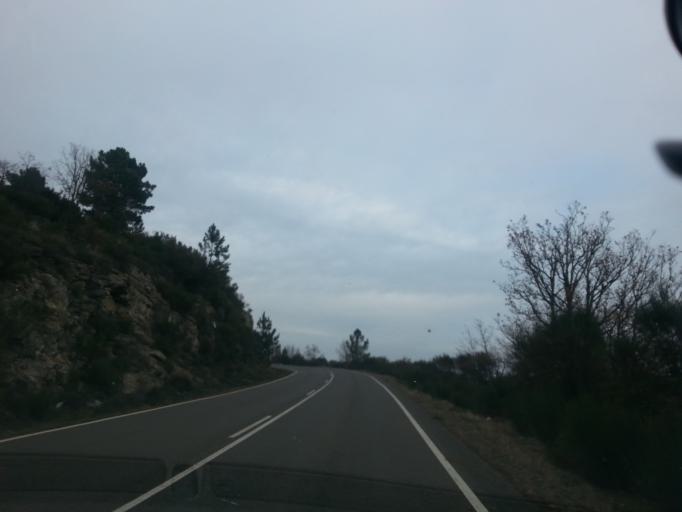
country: ES
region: Castille and Leon
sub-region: Provincia de Salamanca
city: Madronal
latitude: 40.4688
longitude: -6.0608
